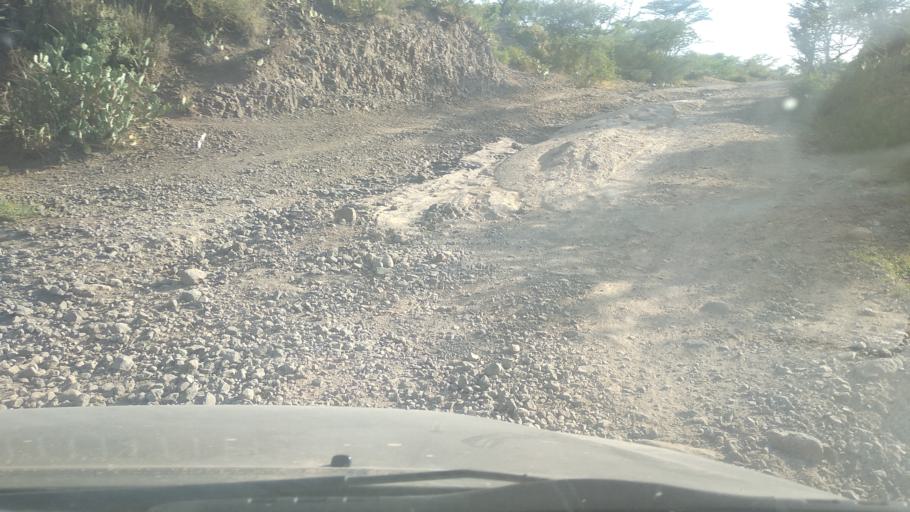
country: ET
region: Oromiya
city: Hirna
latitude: 9.4369
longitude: 40.9843
